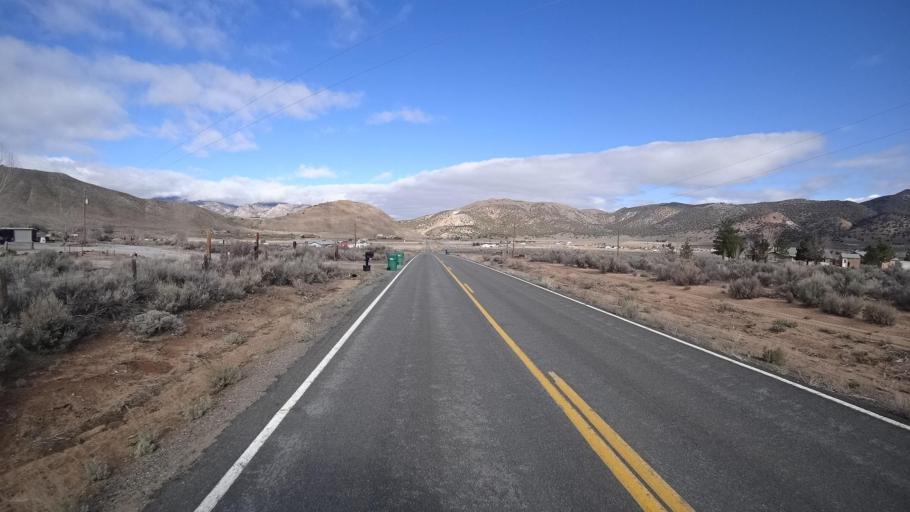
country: US
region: Nevada
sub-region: Washoe County
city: Cold Springs
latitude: 39.8927
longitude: -119.9771
